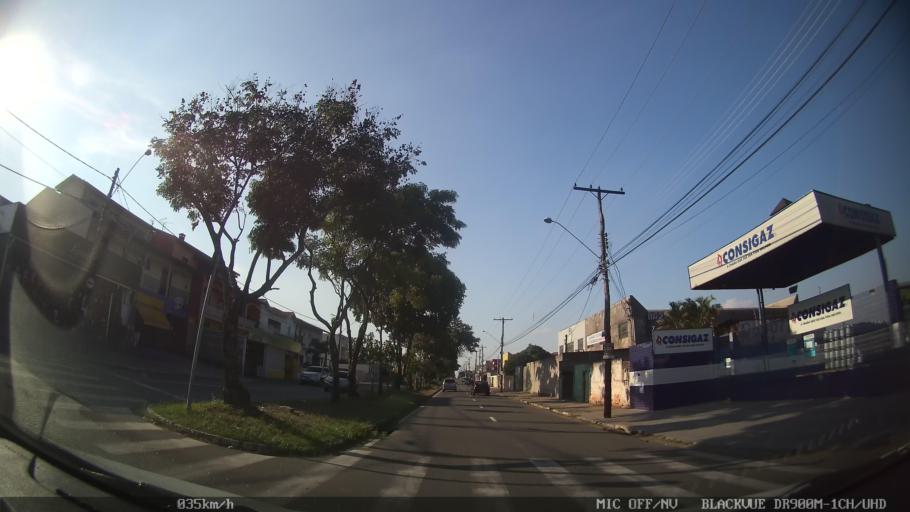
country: BR
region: Sao Paulo
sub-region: Campinas
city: Campinas
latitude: -22.9762
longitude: -47.1475
